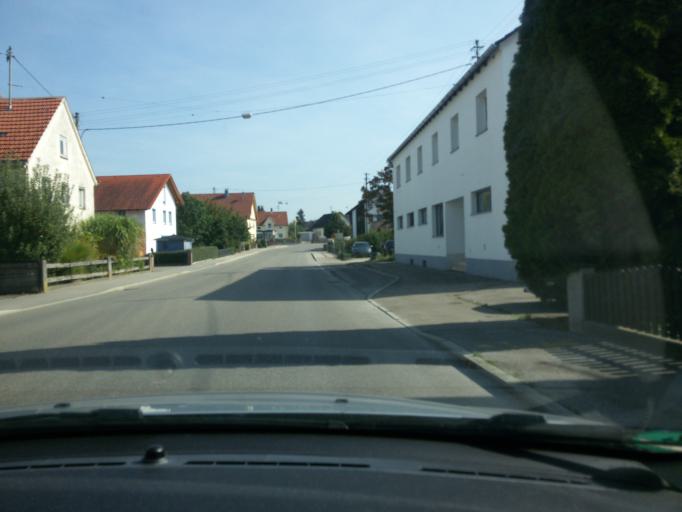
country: DE
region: Bavaria
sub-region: Swabia
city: Ziemetshausen
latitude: 48.2932
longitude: 10.5333
